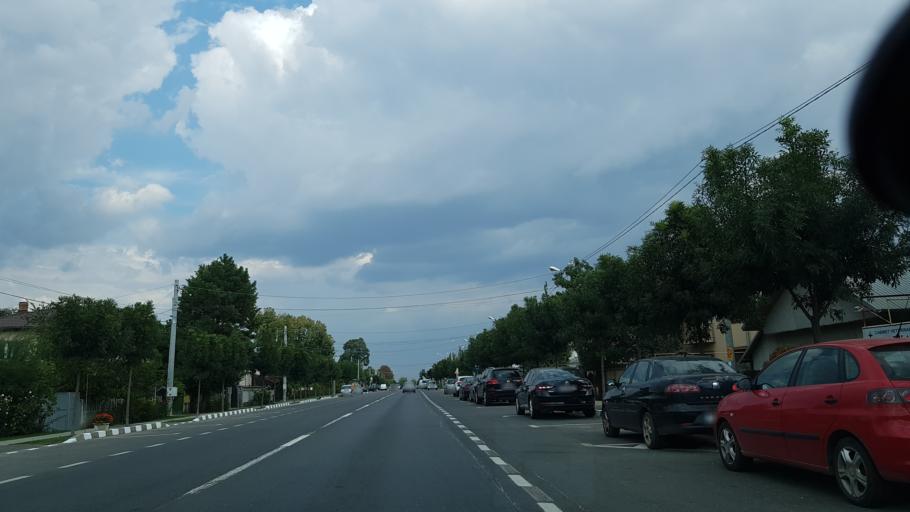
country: RO
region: Ilfov
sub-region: Comuna Branesti
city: Branesti
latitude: 44.4630
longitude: 26.3329
